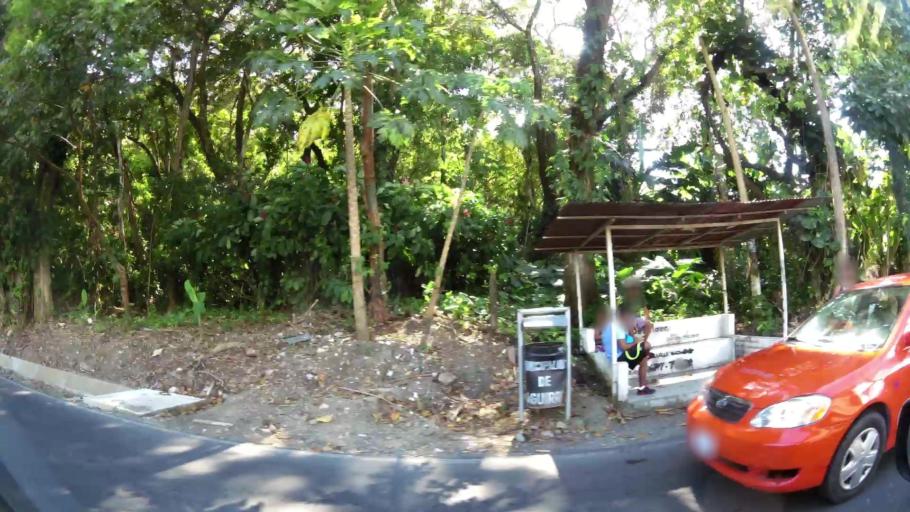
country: CR
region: Puntarenas
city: Quepos
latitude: 9.4282
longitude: -84.1585
